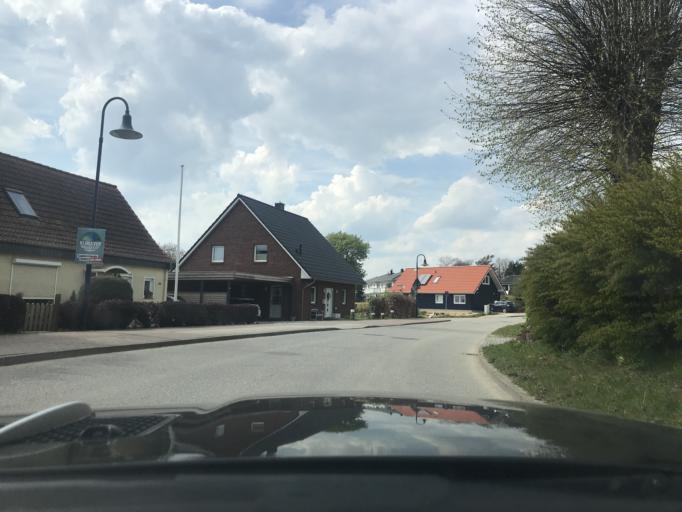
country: DE
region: Schleswig-Holstein
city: Schashagen
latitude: 54.0980
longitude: 10.8857
